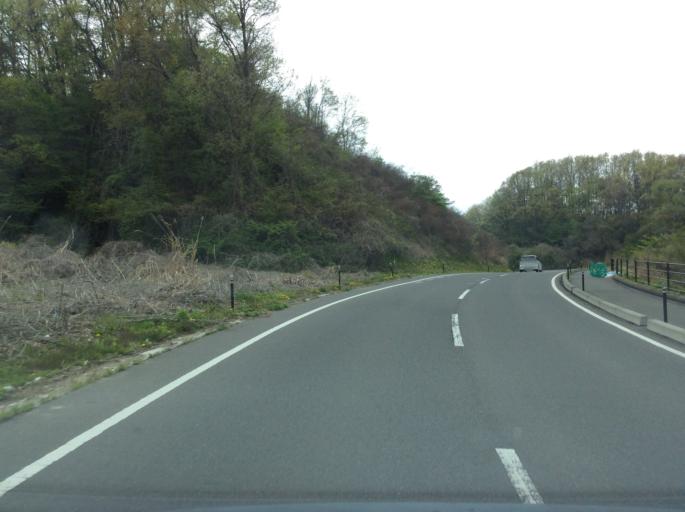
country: JP
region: Fukushima
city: Miharu
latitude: 37.4023
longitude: 140.5322
